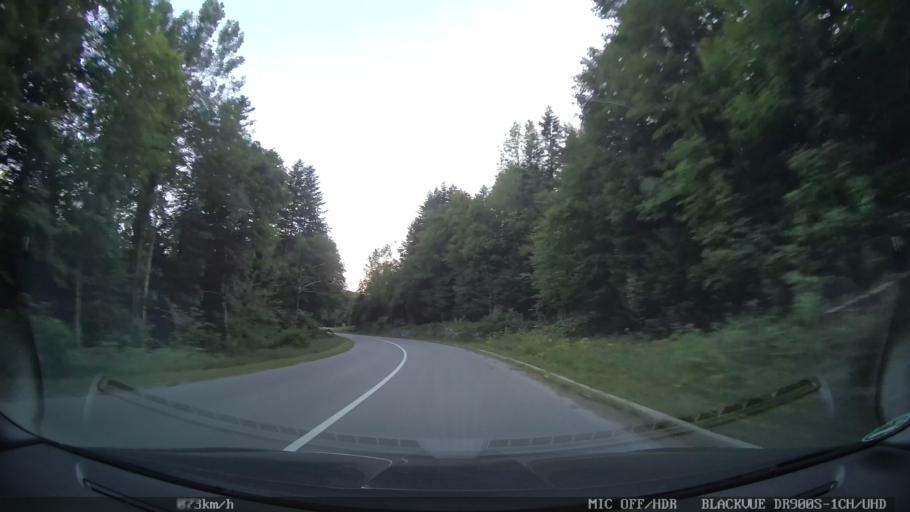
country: HR
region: Primorsko-Goranska
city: Novi Vinodolski
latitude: 45.1700
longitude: 14.9649
